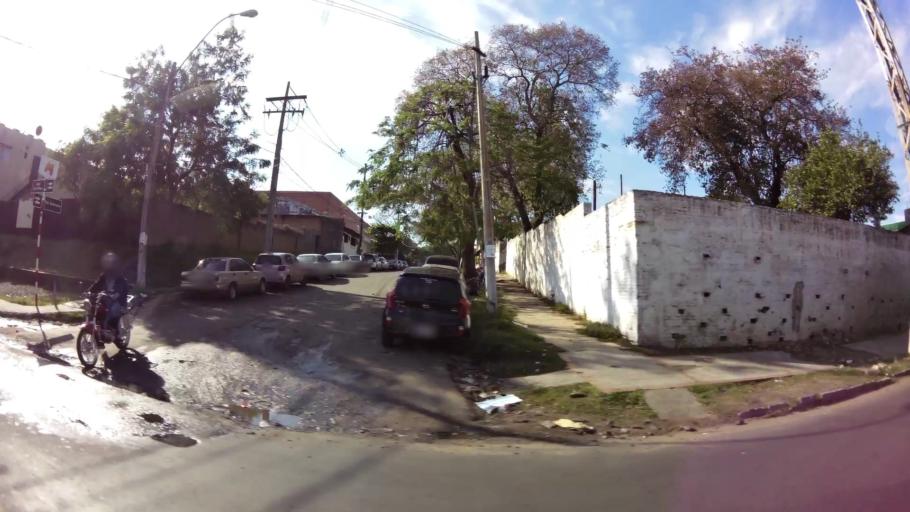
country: PY
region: Asuncion
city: Asuncion
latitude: -25.2742
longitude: -57.6080
